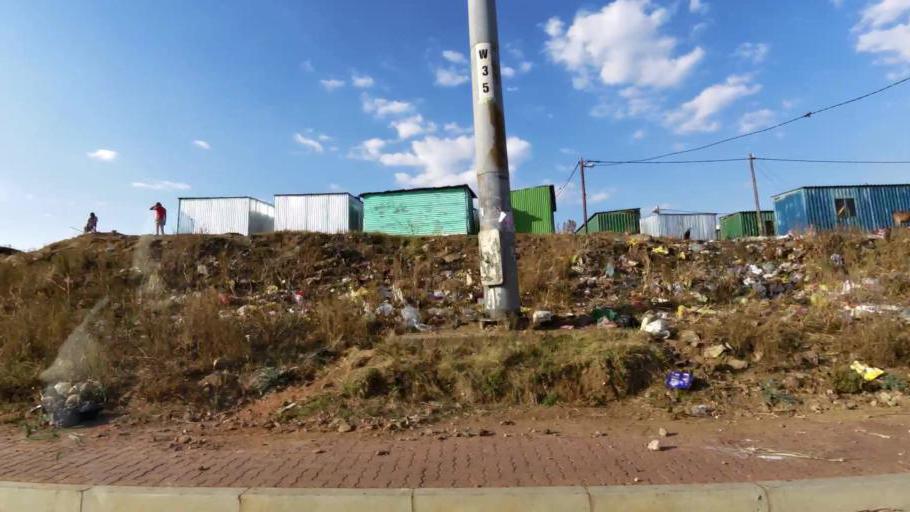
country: ZA
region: Gauteng
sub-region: City of Johannesburg Metropolitan Municipality
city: Soweto
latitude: -26.2321
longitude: 27.8930
